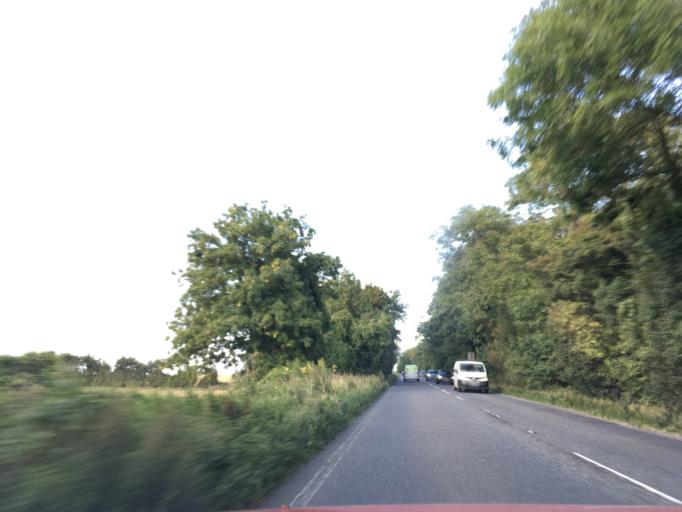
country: GB
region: England
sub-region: Gloucestershire
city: Bourton on the Water
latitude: 51.8759
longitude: -1.7836
